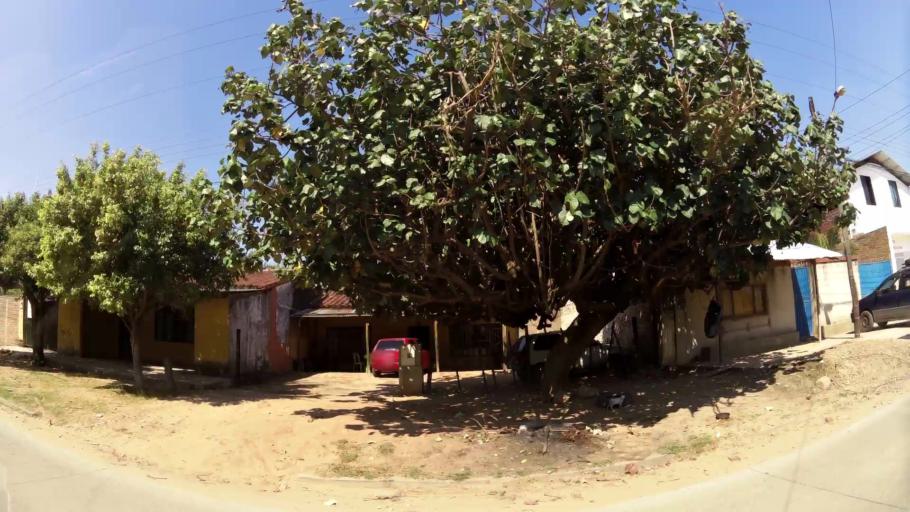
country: BO
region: Santa Cruz
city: Santa Cruz de la Sierra
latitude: -17.7461
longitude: -63.1453
